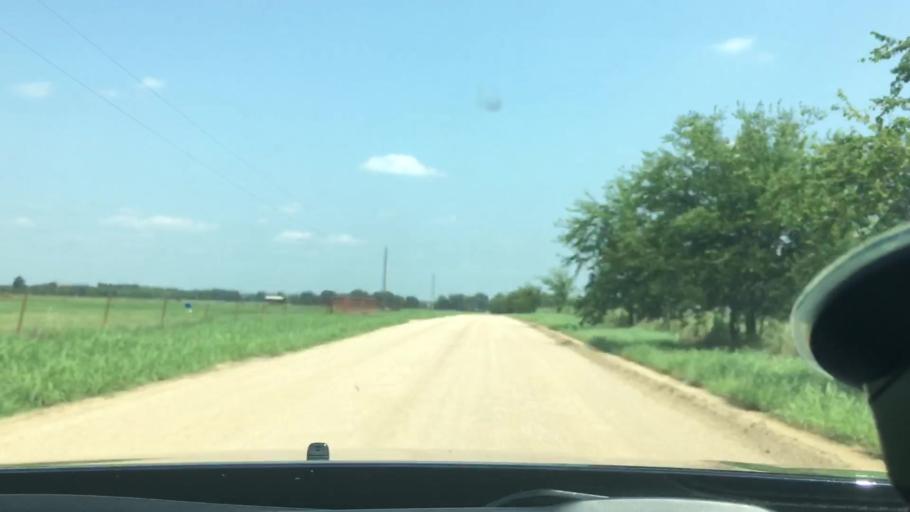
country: US
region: Oklahoma
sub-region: Coal County
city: Coalgate
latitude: 34.4330
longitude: -96.4303
